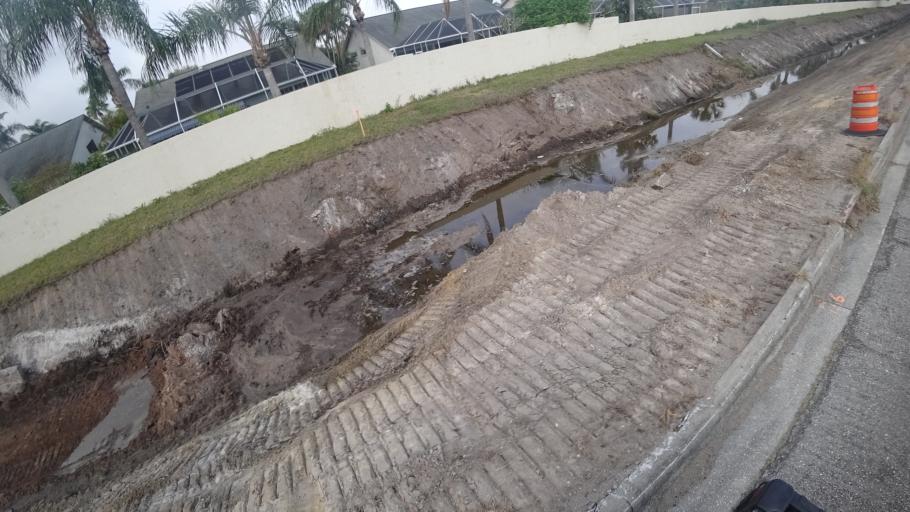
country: US
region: Florida
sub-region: Manatee County
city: Samoset
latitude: 27.4556
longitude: -82.5056
